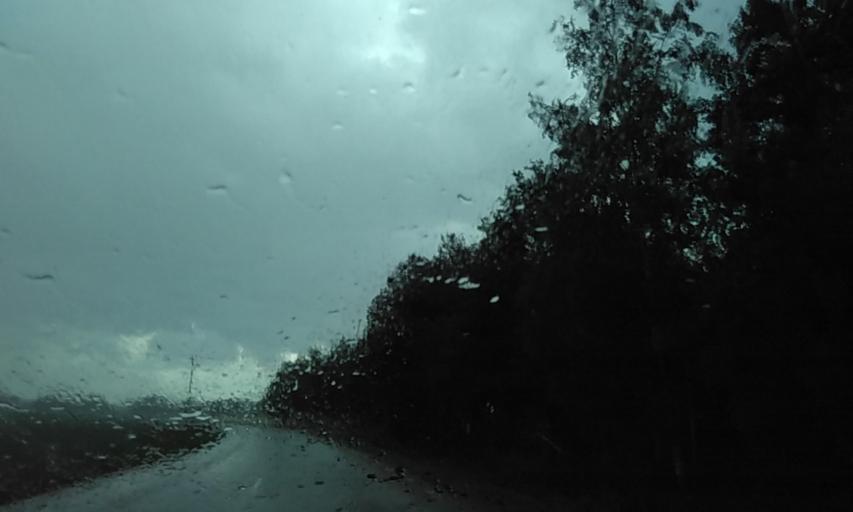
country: SE
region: Vaestra Goetaland
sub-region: Lidkopings Kommun
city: Lidkoping
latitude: 58.5036
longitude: 12.9403
